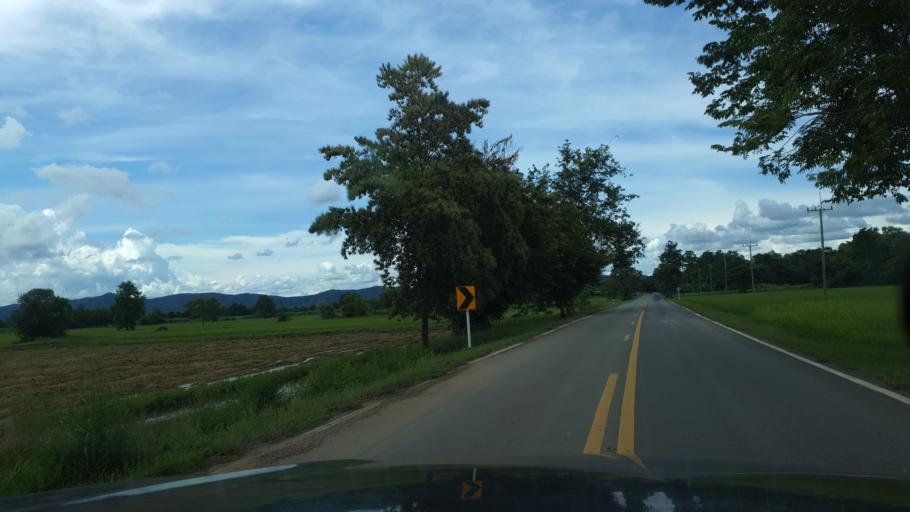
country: TH
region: Sukhothai
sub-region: Amphoe Si Satchanalai
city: Si Satchanalai
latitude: 17.4705
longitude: 99.7550
